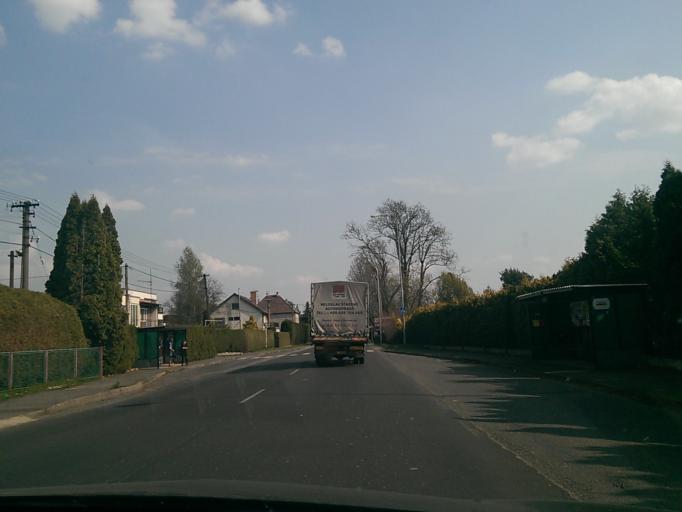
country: CZ
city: Ohrazenice
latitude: 50.5938
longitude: 15.1255
